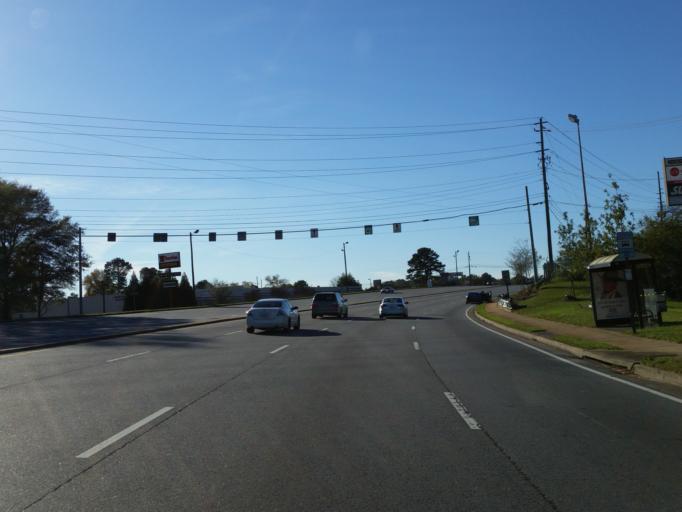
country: US
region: Georgia
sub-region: Cobb County
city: Fair Oaks
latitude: 33.9395
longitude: -84.5086
